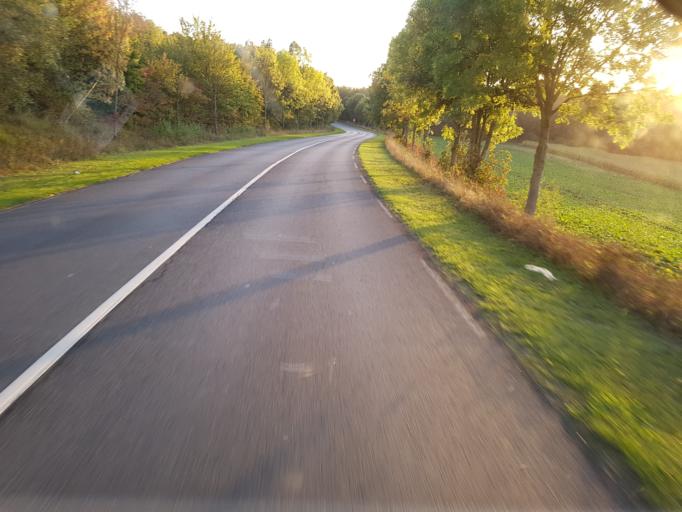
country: FR
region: Picardie
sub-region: Departement de la Somme
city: Saleux
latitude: 49.8515
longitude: 2.2366
